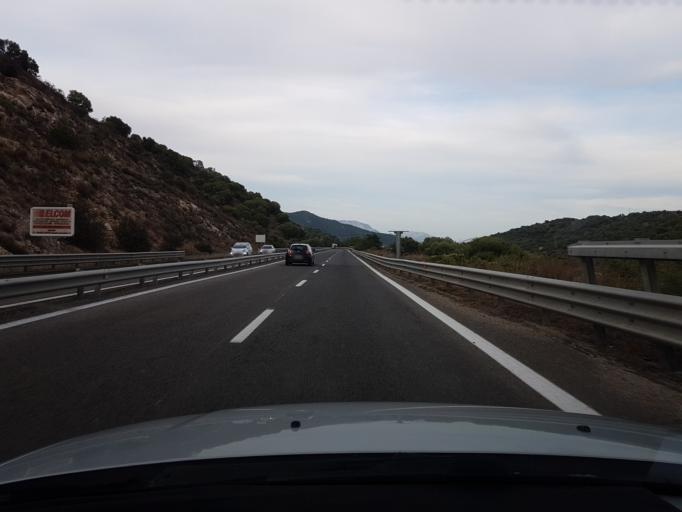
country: IT
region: Sardinia
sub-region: Provincia di Nuoro
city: Nuoro
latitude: 40.3523
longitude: 9.3412
